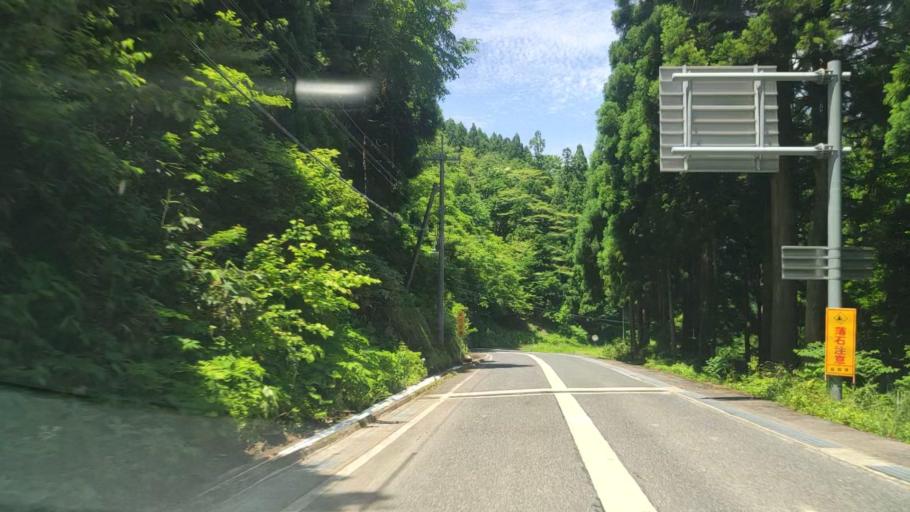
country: JP
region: Tottori
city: Tottori
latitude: 35.3537
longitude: 134.4870
